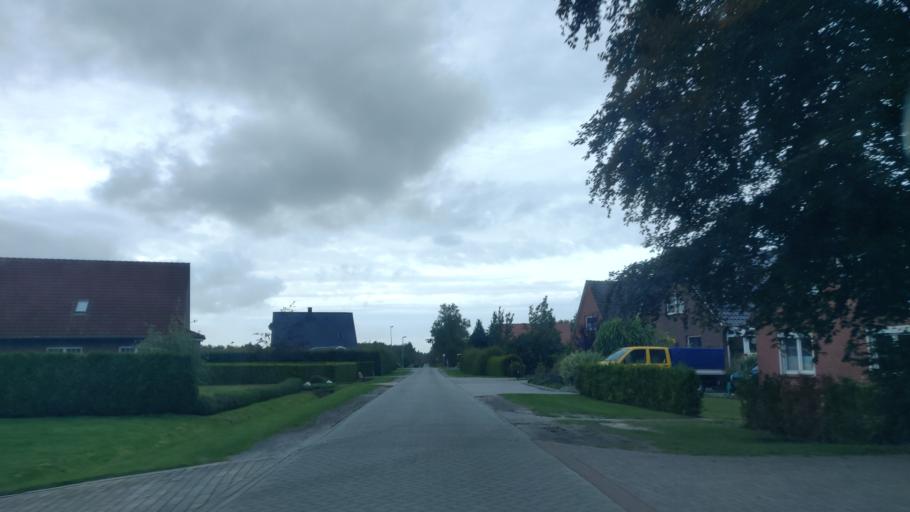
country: DE
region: Lower Saxony
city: Aurich
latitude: 53.4877
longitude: 7.4236
